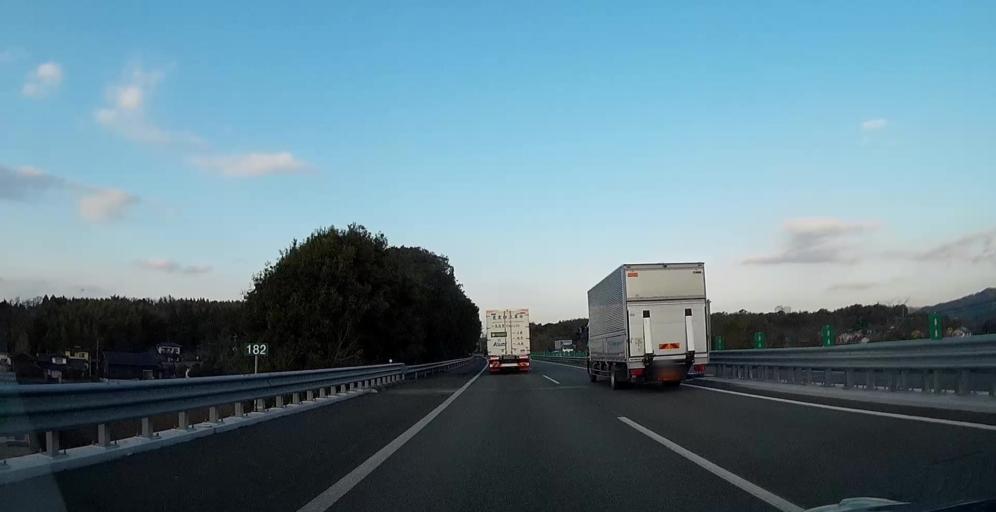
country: JP
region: Kumamoto
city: Kumamoto
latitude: 32.7432
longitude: 130.7846
